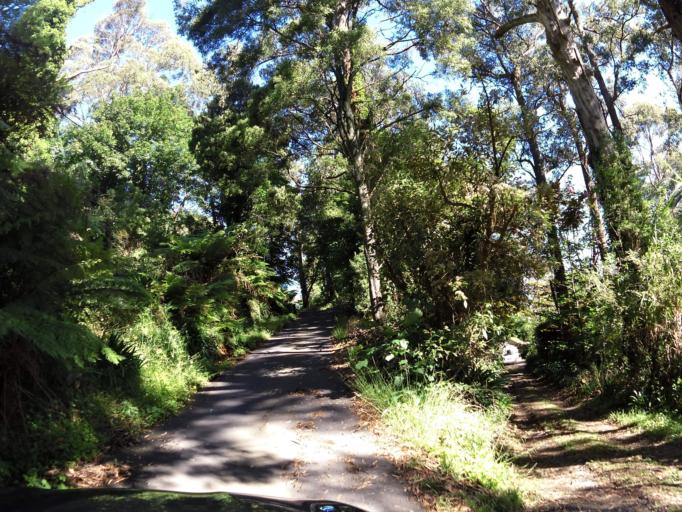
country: AU
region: Victoria
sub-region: Yarra Ranges
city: Ferny Creek
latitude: -37.8847
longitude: 145.3292
